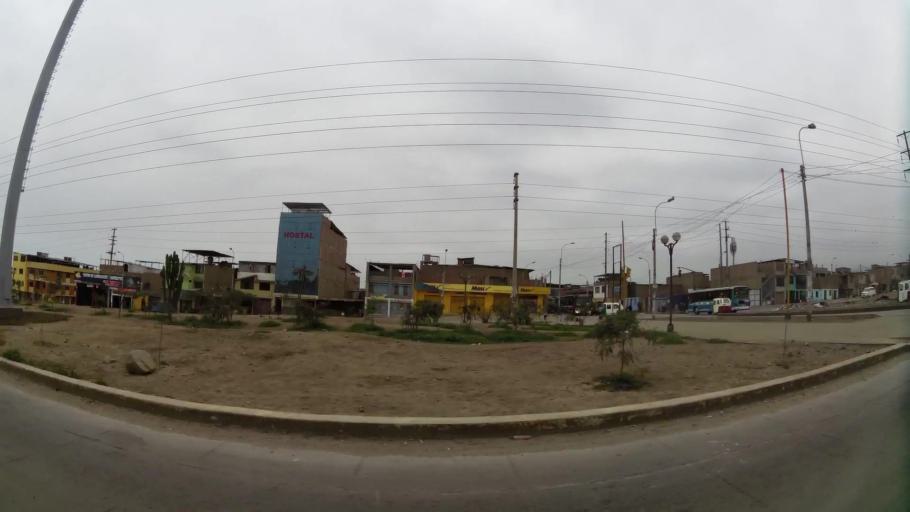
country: PE
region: Lima
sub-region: Lima
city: Surco
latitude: -12.2038
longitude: -76.9493
